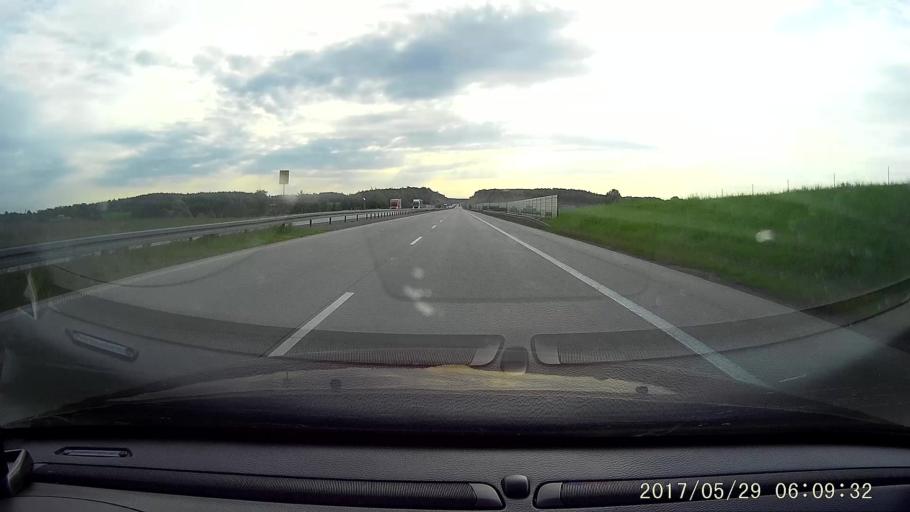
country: PL
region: Lower Silesian Voivodeship
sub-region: Powiat lubanski
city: Pisarzowice
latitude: 51.2098
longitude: 15.1839
